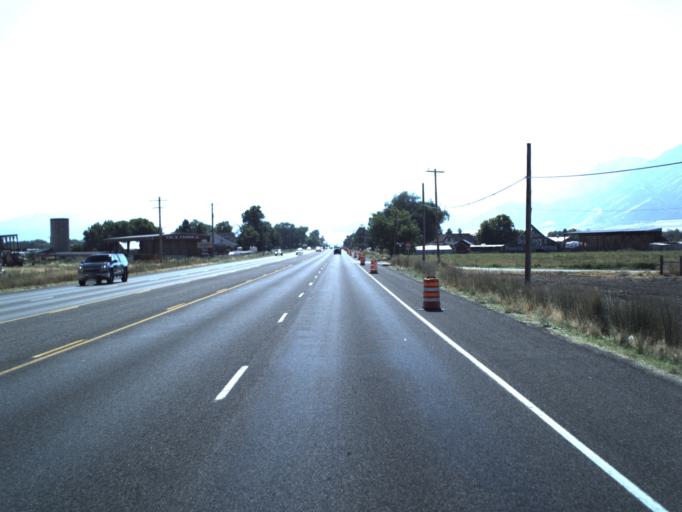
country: US
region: Utah
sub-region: Cache County
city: Nibley
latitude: 41.6877
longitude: -111.8709
